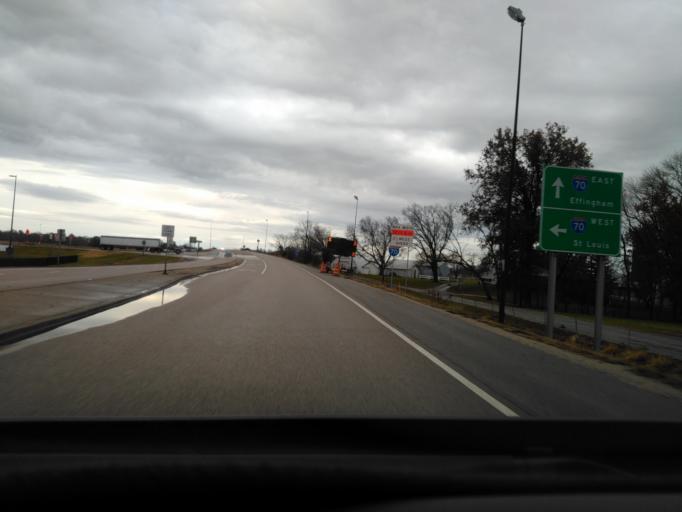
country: US
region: Illinois
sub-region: Bond County
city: Greenville
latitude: 38.8736
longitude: -89.3885
